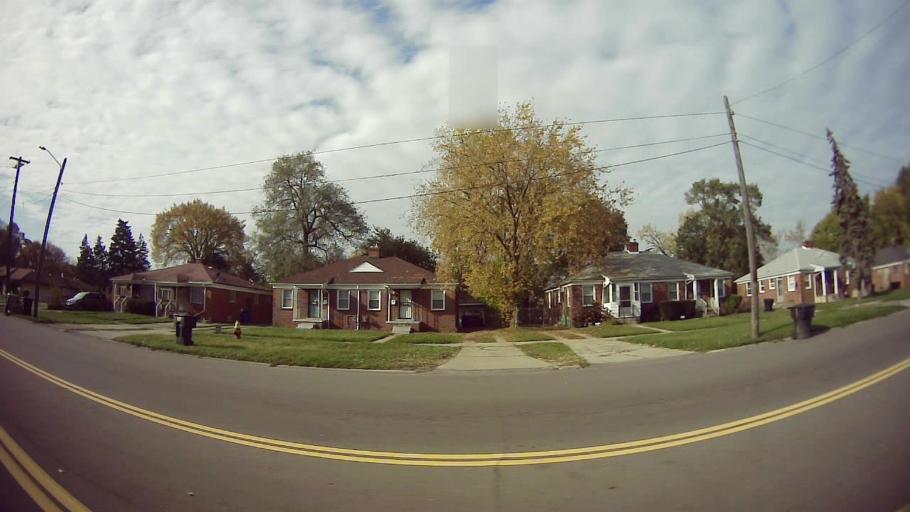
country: US
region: Michigan
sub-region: Oakland County
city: Oak Park
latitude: 42.4356
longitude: -83.1806
